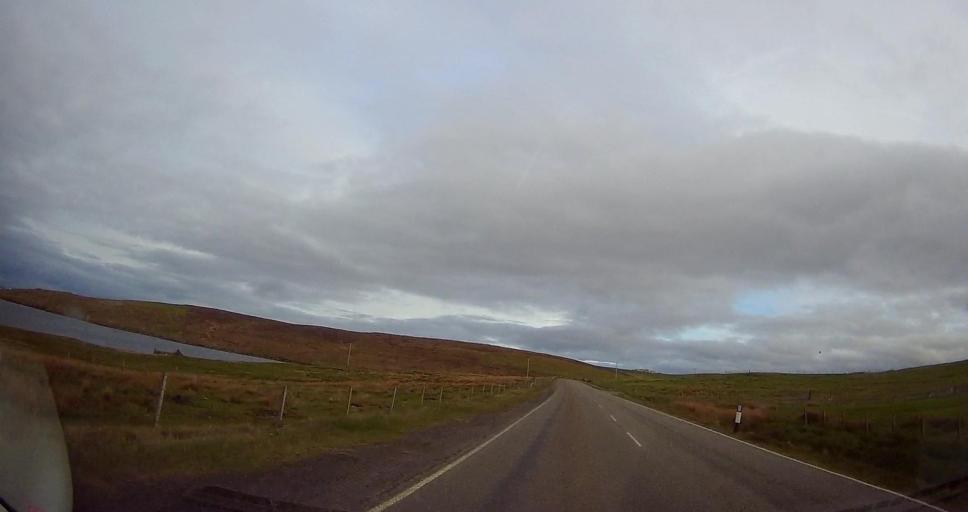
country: GB
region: Scotland
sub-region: Shetland Islands
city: Lerwick
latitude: 60.4648
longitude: -1.2123
